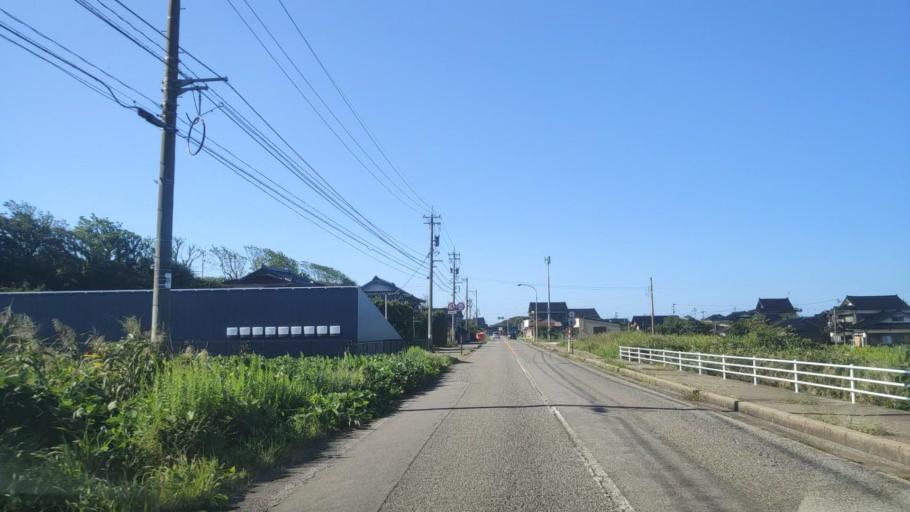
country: JP
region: Ishikawa
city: Hakui
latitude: 36.9522
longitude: 136.7666
